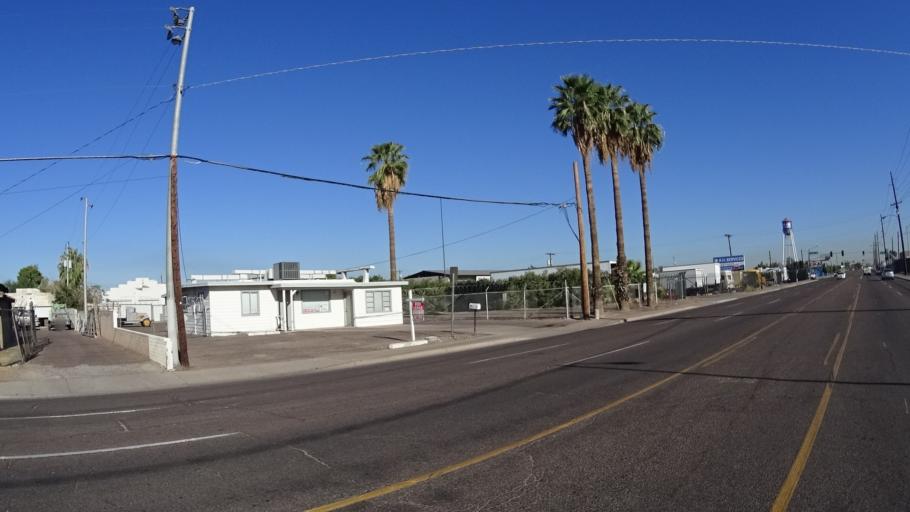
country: US
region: Arizona
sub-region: Maricopa County
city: Phoenix
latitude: 33.4406
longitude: -112.1174
